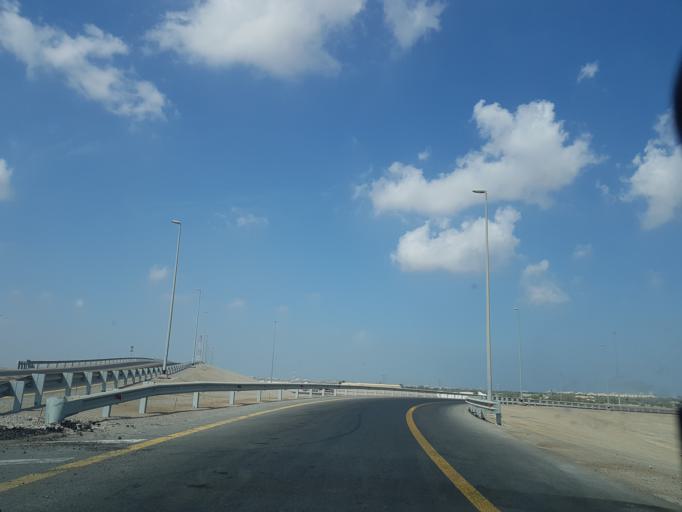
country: AE
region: Ra's al Khaymah
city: Ras al-Khaimah
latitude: 25.7167
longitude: 56.0092
